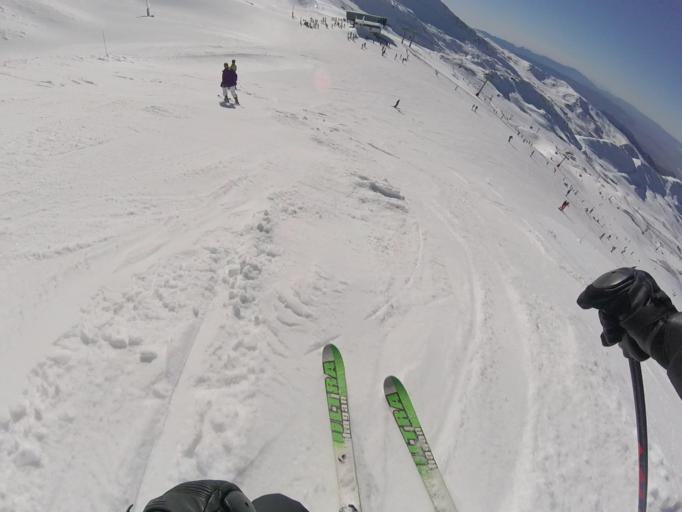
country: ES
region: Andalusia
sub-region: Provincia de Granada
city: Capileira
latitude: 37.0634
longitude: -3.3740
